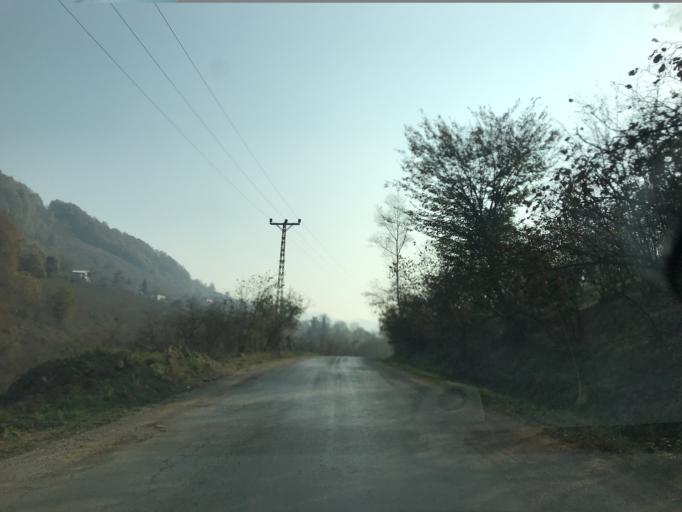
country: TR
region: Duzce
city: Cumayeri
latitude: 40.9173
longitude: 30.9324
